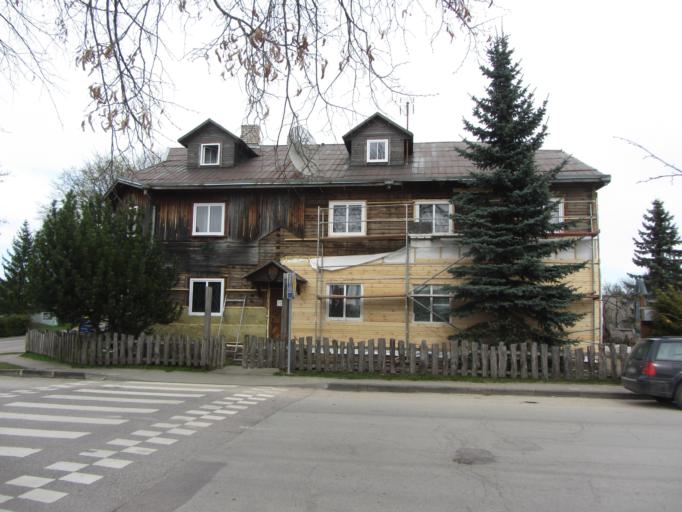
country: LT
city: Zarasai
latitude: 55.5812
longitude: 26.1332
